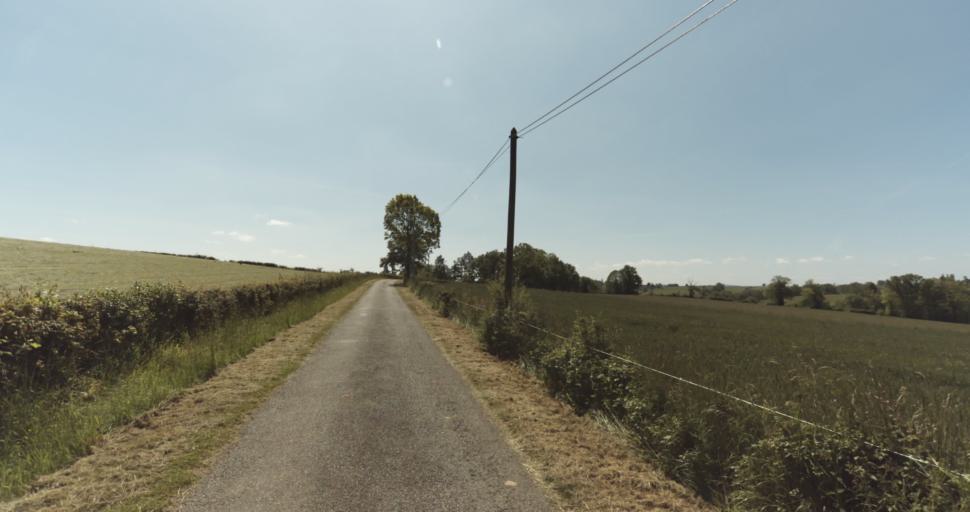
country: FR
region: Limousin
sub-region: Departement de la Haute-Vienne
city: Le Vigen
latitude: 45.7342
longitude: 1.2916
